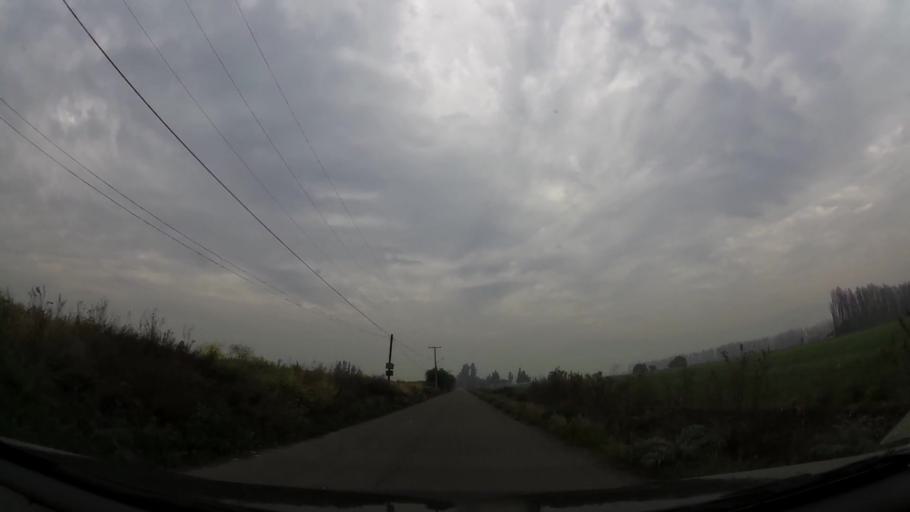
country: CL
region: Santiago Metropolitan
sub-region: Provincia de Chacabuco
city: Chicureo Abajo
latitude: -33.2610
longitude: -70.7638
